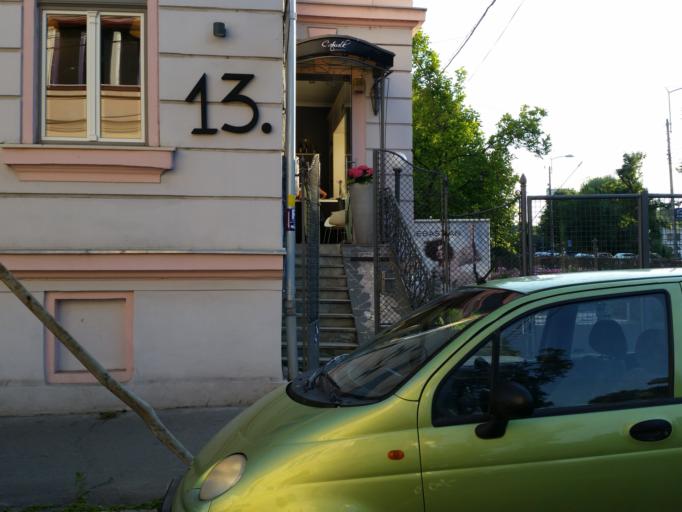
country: RO
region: Cluj
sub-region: Municipiul Cluj-Napoca
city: Cluj-Napoca
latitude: 46.7683
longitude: 23.5796
